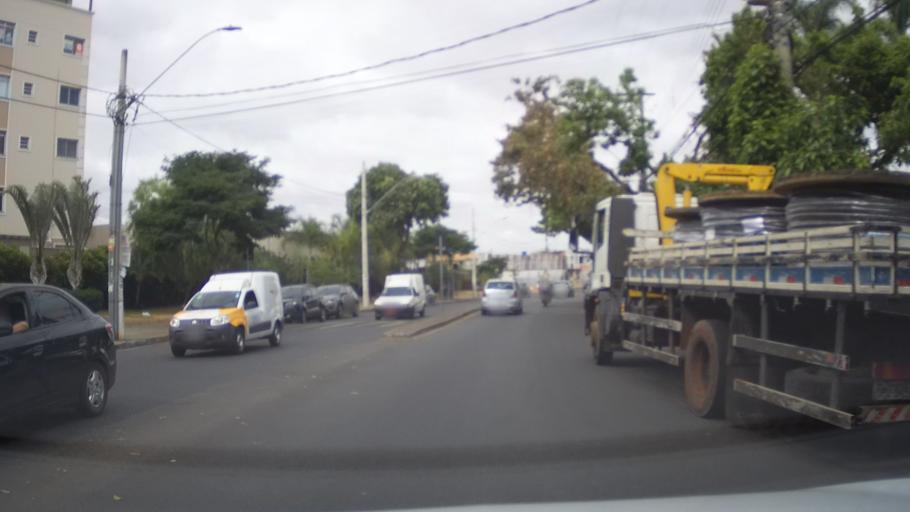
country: BR
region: Minas Gerais
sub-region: Belo Horizonte
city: Belo Horizonte
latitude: -19.8440
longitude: -43.9538
